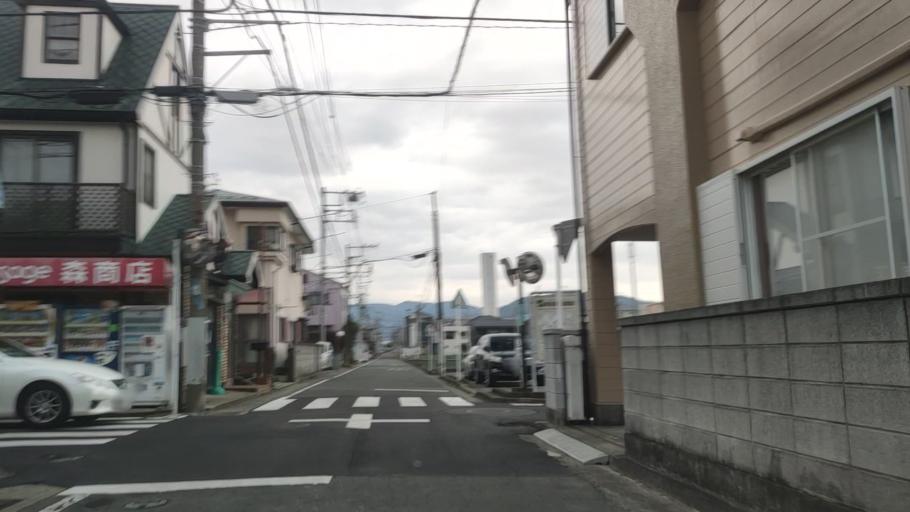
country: JP
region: Kanagawa
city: Odawara
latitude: 35.2728
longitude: 139.1966
